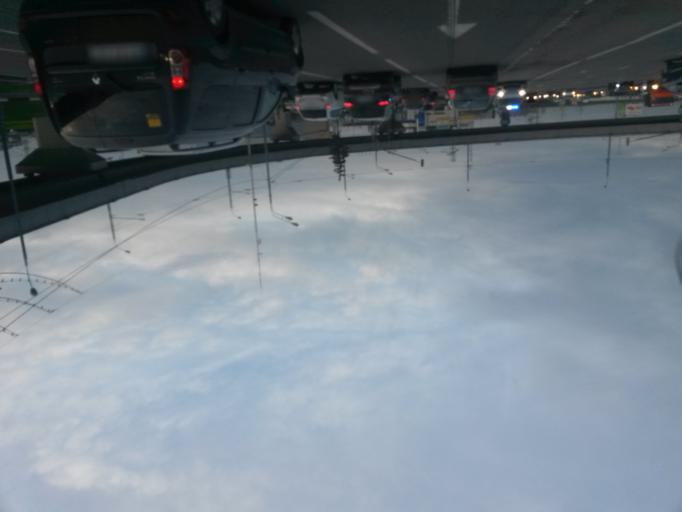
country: RU
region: Moscow
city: Annino
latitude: 55.5795
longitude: 37.5963
